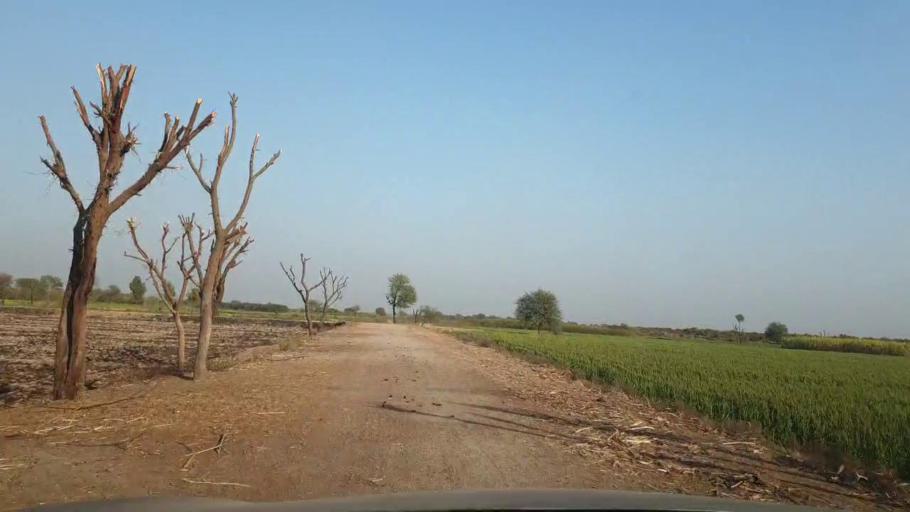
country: PK
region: Sindh
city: Tando Allahyar
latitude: 25.5864
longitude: 68.6751
